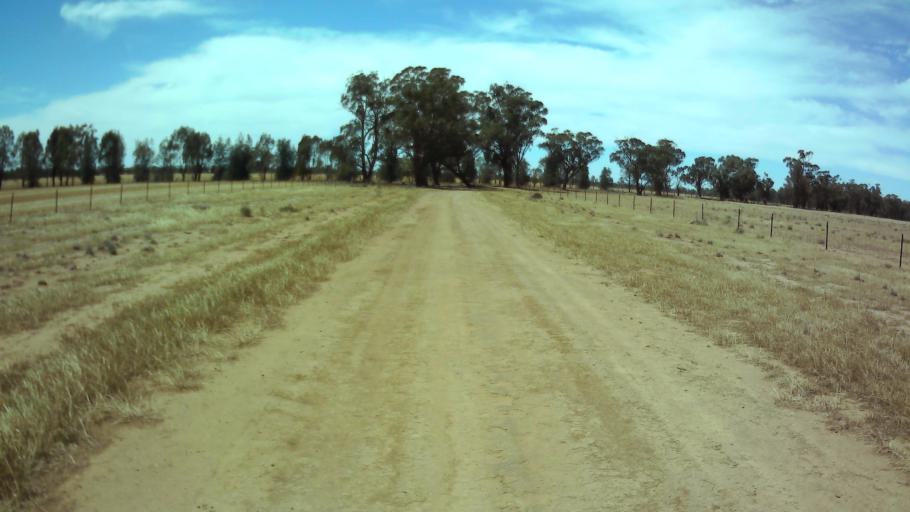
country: AU
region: New South Wales
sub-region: Weddin
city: Grenfell
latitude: -33.9029
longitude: 147.8069
